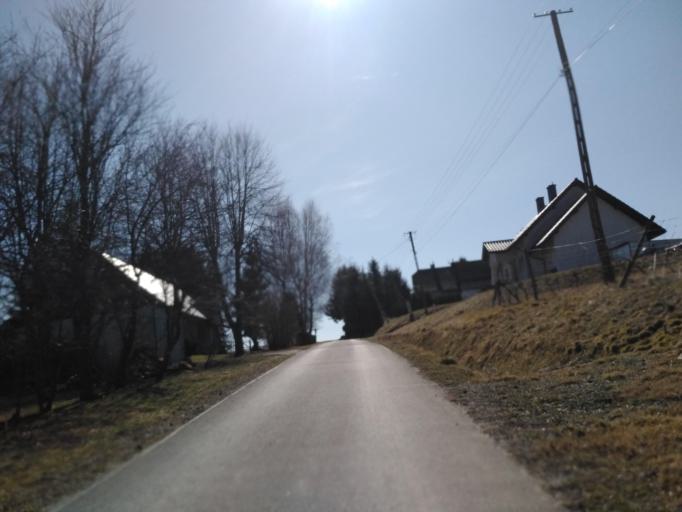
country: PL
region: Subcarpathian Voivodeship
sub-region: Powiat brzozowski
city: Jasienica Rosielna
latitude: 49.7630
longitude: 21.9517
